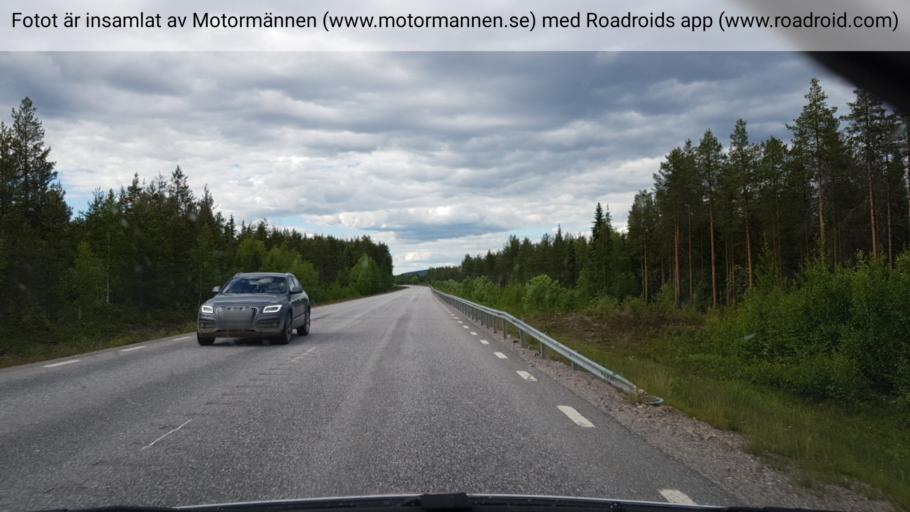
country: SE
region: Norrbotten
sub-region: Overkalix Kommun
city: OEverkalix
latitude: 66.6373
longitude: 22.2021
